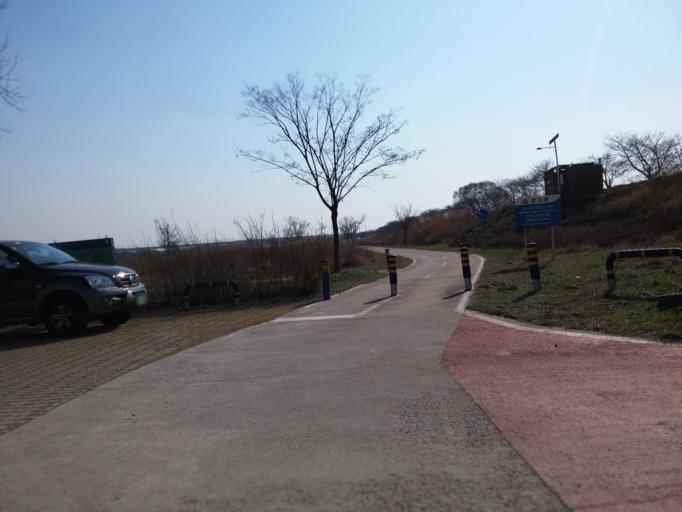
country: KR
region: Chungcheongbuk-do
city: Cheongju-si
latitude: 36.6206
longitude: 127.3475
